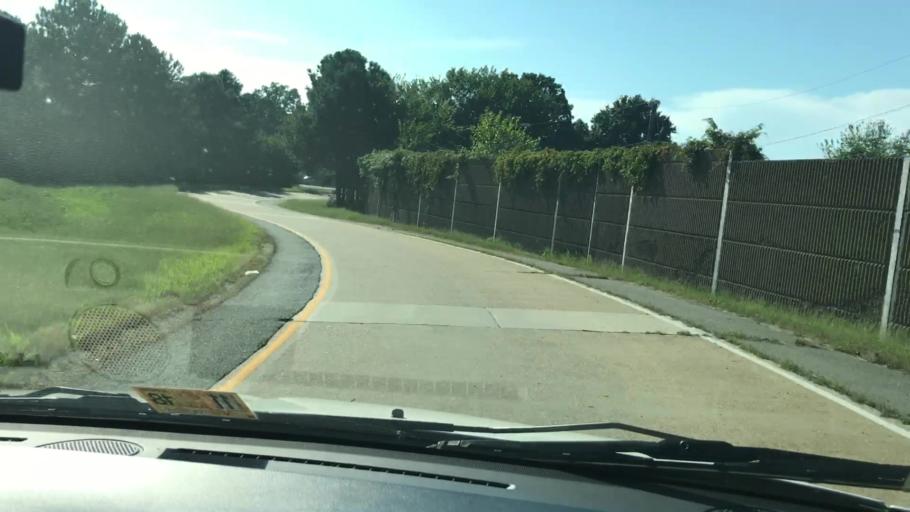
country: US
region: Virginia
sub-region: City of Norfolk
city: Norfolk
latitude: 36.8931
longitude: -76.2304
